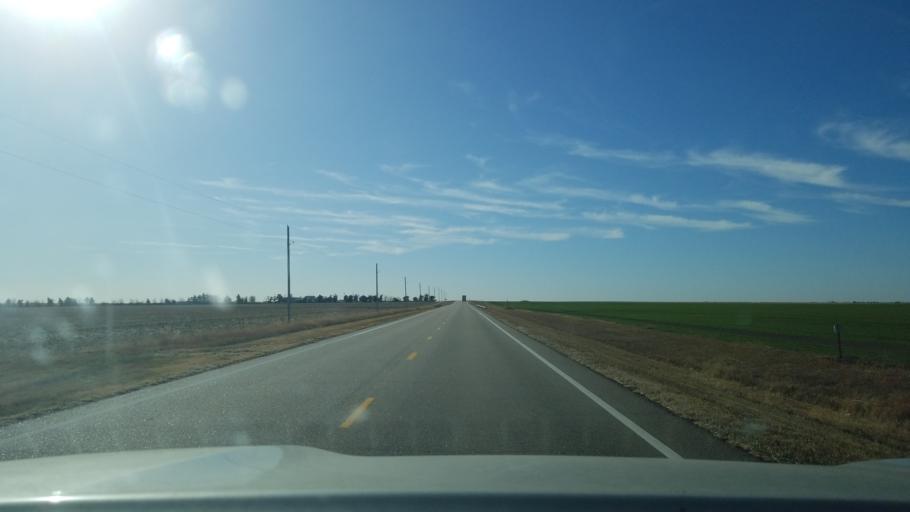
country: US
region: Kansas
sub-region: Ness County
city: Ness City
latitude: 38.3907
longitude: -99.8979
